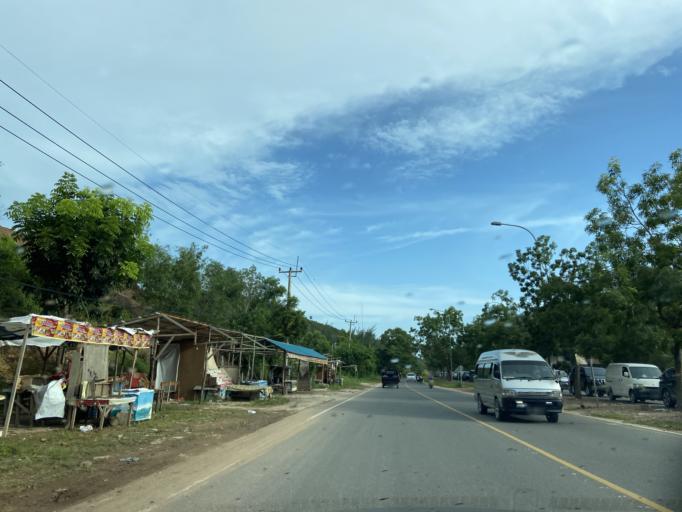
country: SG
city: Singapore
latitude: 0.9844
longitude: 104.0392
